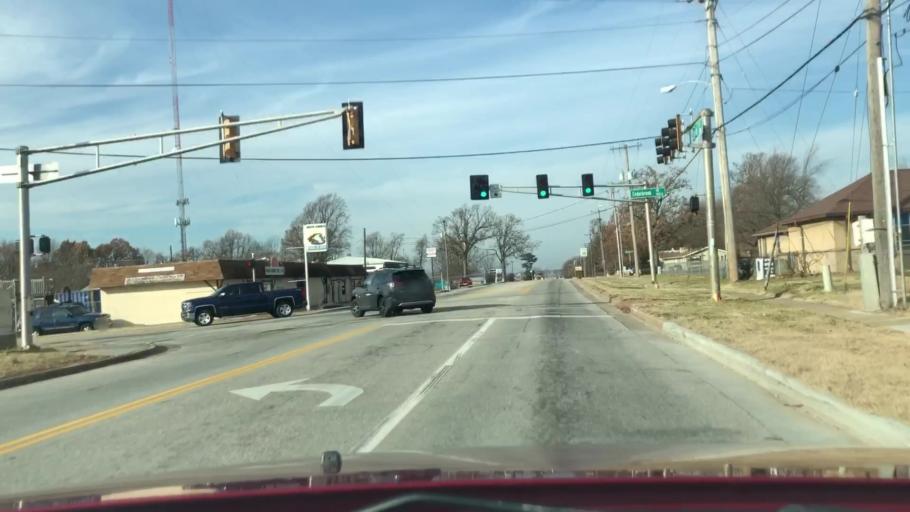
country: US
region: Missouri
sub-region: Greene County
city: Springfield
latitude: 37.2247
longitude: -93.2385
